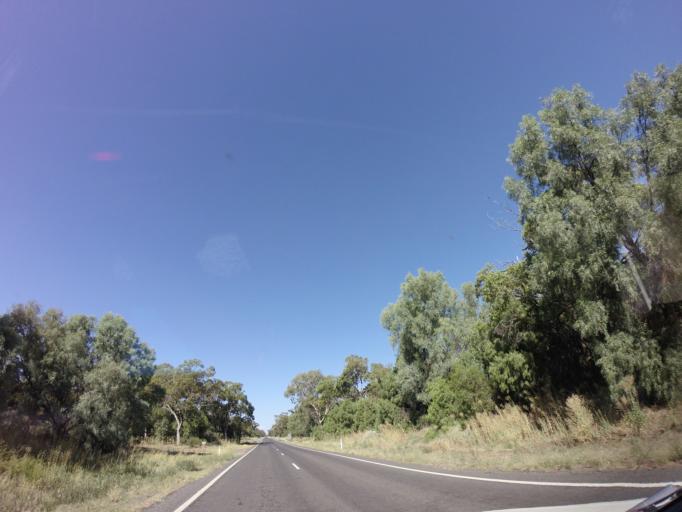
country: AU
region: New South Wales
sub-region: Narromine
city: Narromine
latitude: -31.6549
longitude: 147.8793
